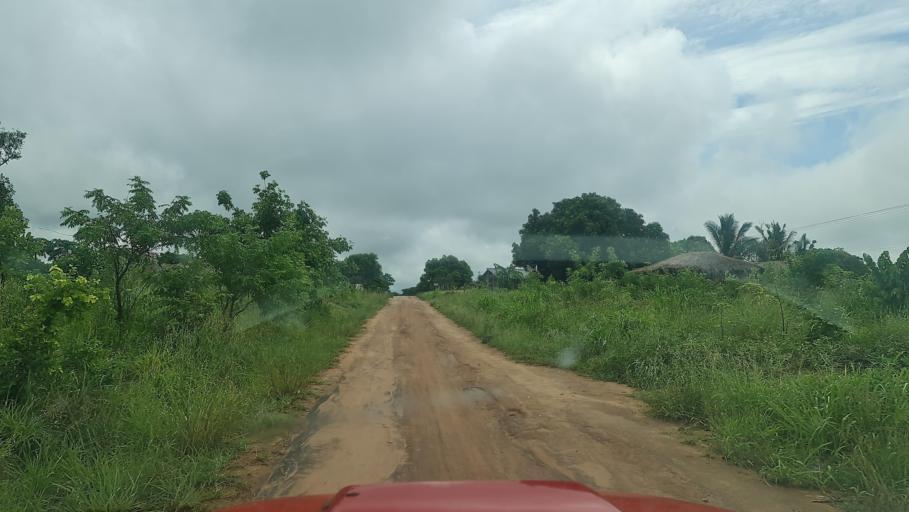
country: MW
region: Southern Region
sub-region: Nsanje District
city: Nsanje
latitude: -17.1858
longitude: 35.9209
